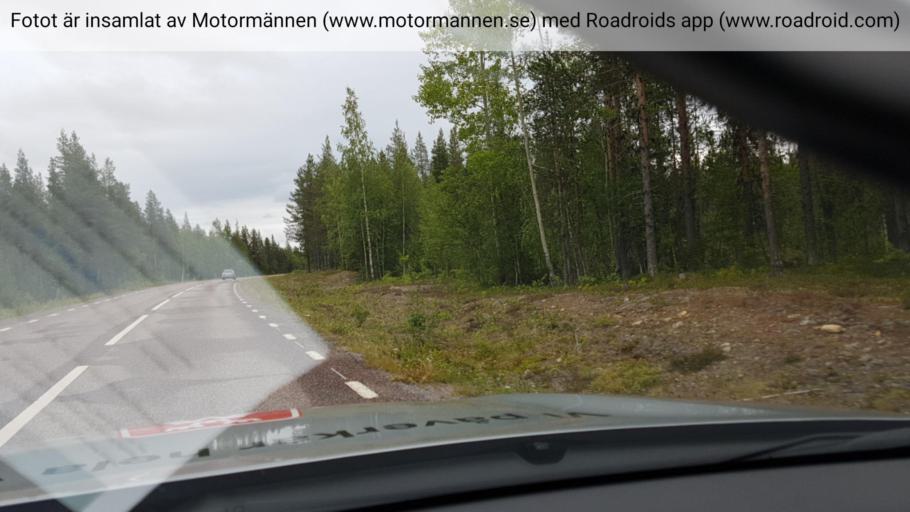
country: SE
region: Norrbotten
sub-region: Gallivare Kommun
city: Gaellivare
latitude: 67.0621
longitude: 21.5735
